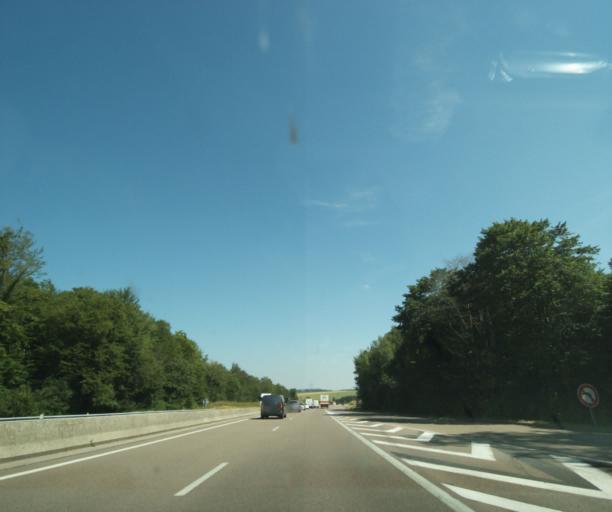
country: FR
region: Lorraine
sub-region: Departement de Meurthe-et-Moselle
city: Colombey-les-Belles
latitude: 48.4264
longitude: 5.8601
